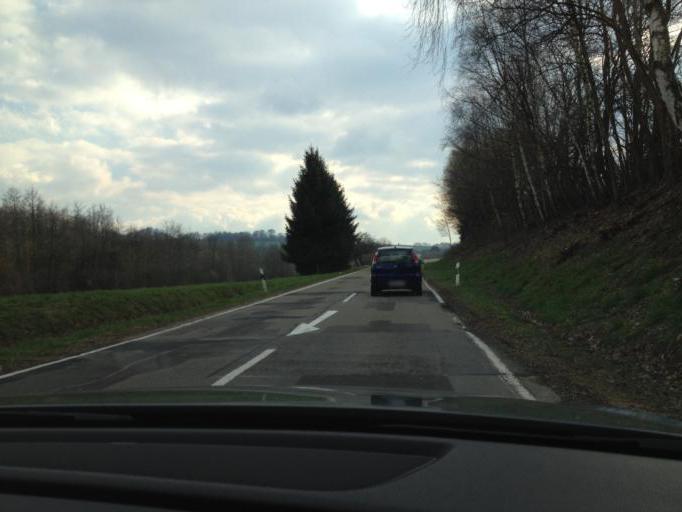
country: DE
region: Saarland
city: Sankt Wendel
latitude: 49.4954
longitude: 7.2173
